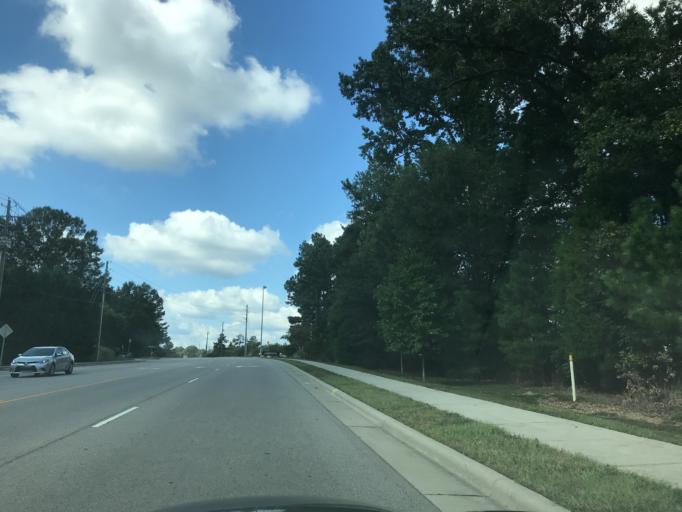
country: US
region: North Carolina
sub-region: Wake County
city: Rolesville
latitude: 35.8815
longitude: -78.5491
